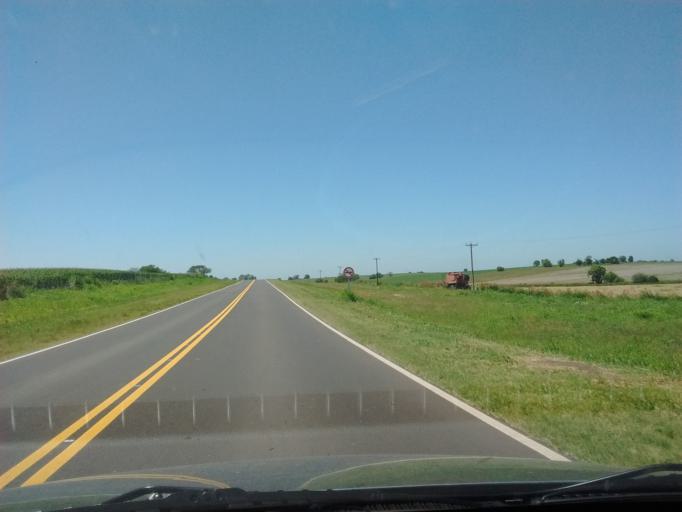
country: AR
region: Entre Rios
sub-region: Departamento de Victoria
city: Victoria
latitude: -32.8120
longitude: -59.8854
